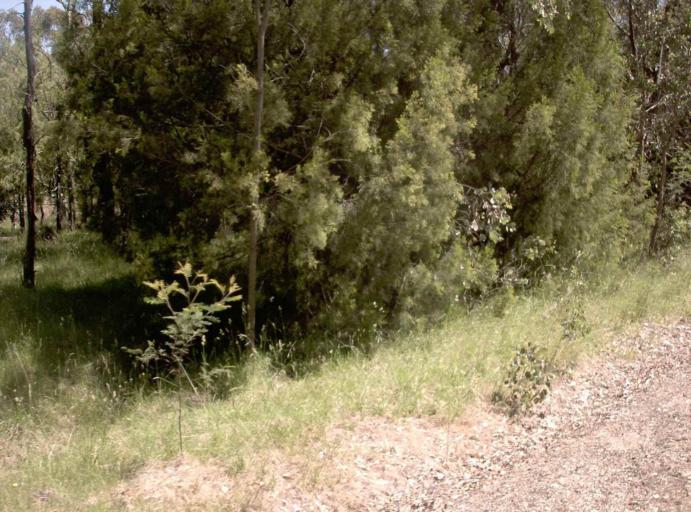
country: AU
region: Victoria
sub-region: East Gippsland
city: Lakes Entrance
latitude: -37.3336
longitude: 148.2328
